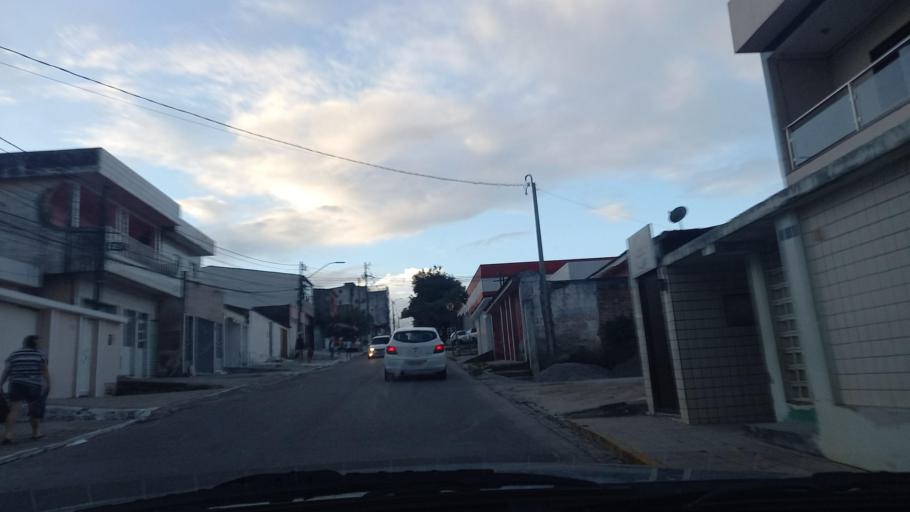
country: BR
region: Pernambuco
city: Garanhuns
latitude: -8.8837
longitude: -36.4663
